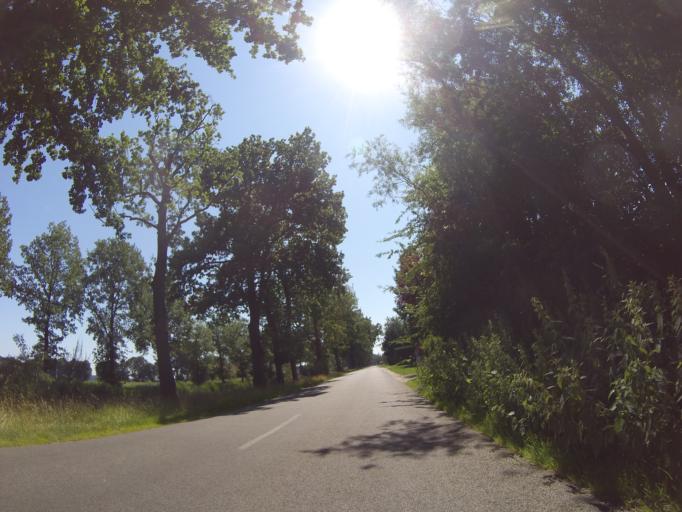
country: NL
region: Drenthe
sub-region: Gemeente Coevorden
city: Sleen
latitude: 52.8445
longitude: 6.7838
